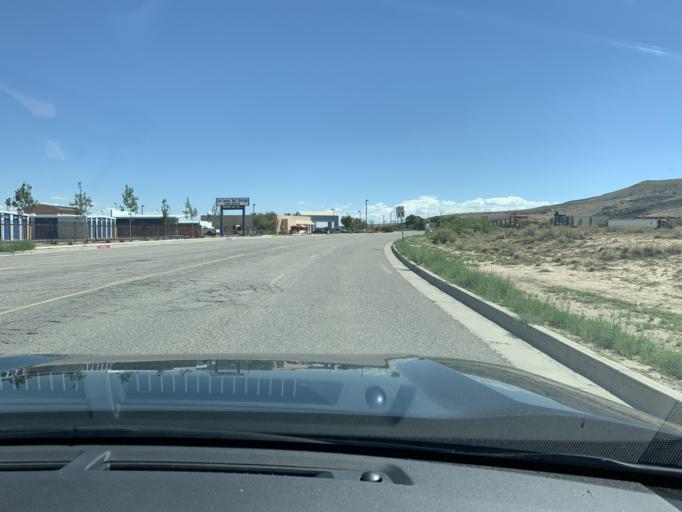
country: US
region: New Mexico
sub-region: Valencia County
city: Los Lunas
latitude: 34.8200
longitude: -106.7684
